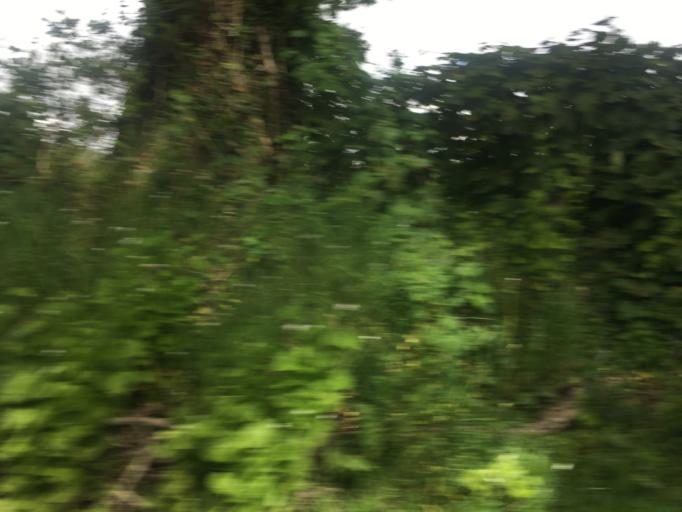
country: GB
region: Wales
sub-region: County of Ceredigion
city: Lampeter
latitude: 52.1359
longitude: -4.0740
